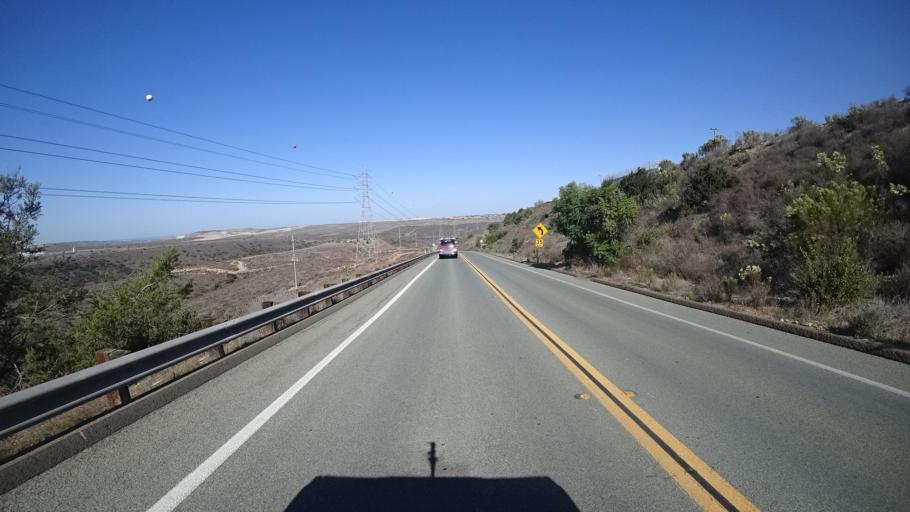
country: MX
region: Baja California
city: Tijuana
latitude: 32.5900
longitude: -116.9233
